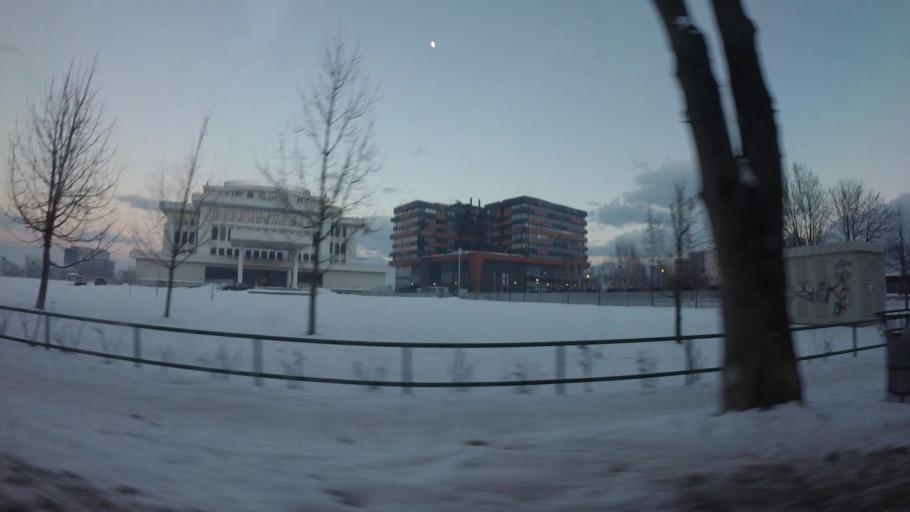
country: BA
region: Federation of Bosnia and Herzegovina
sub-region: Kanton Sarajevo
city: Sarajevo
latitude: 43.8237
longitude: 18.3074
